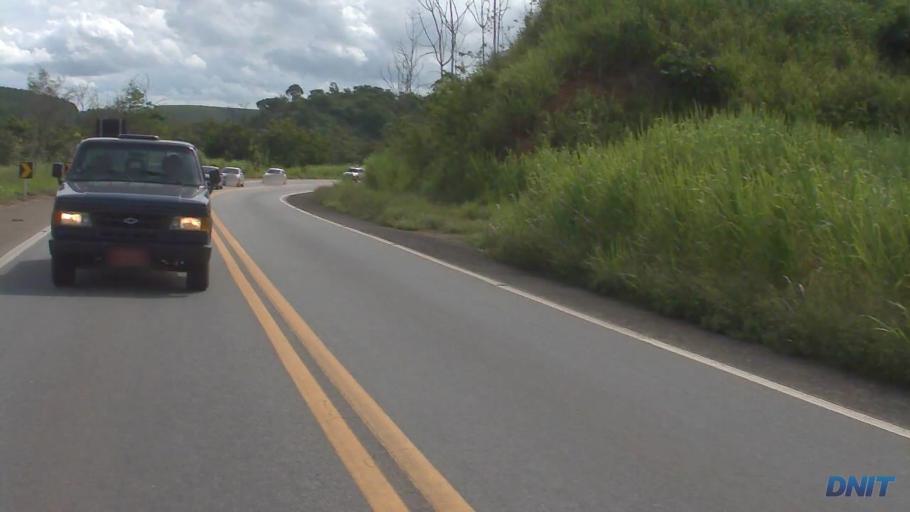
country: BR
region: Minas Gerais
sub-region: Ipaba
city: Ipaba
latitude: -19.3871
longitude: -42.4757
